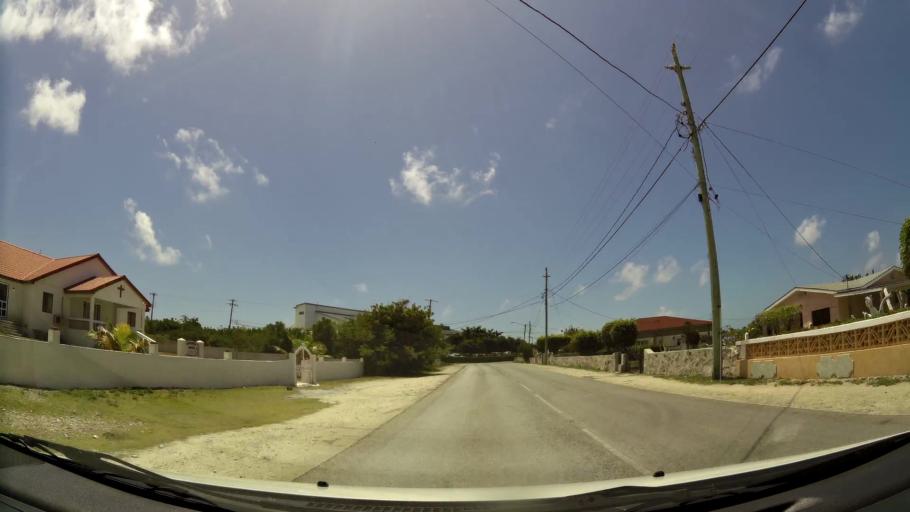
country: TC
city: Cockburn Town
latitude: 21.4813
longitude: -71.1445
